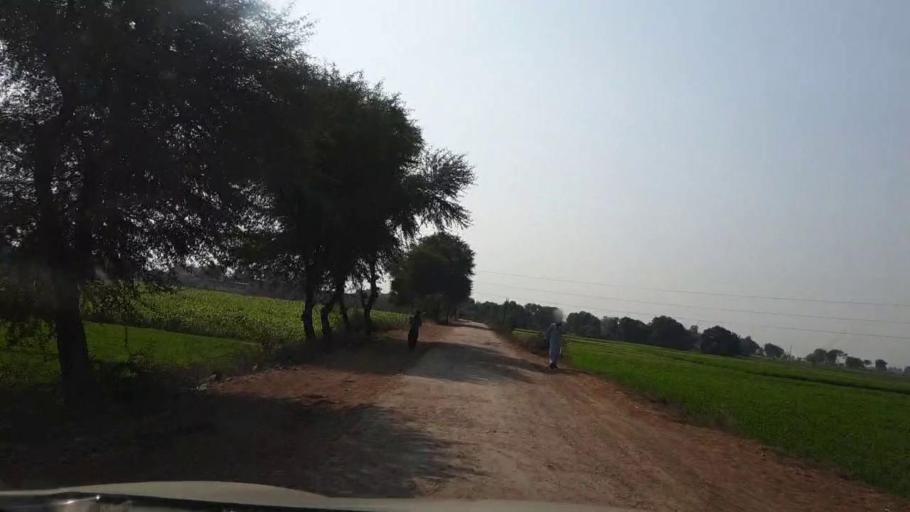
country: PK
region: Sindh
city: Bhit Shah
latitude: 25.7498
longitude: 68.5052
